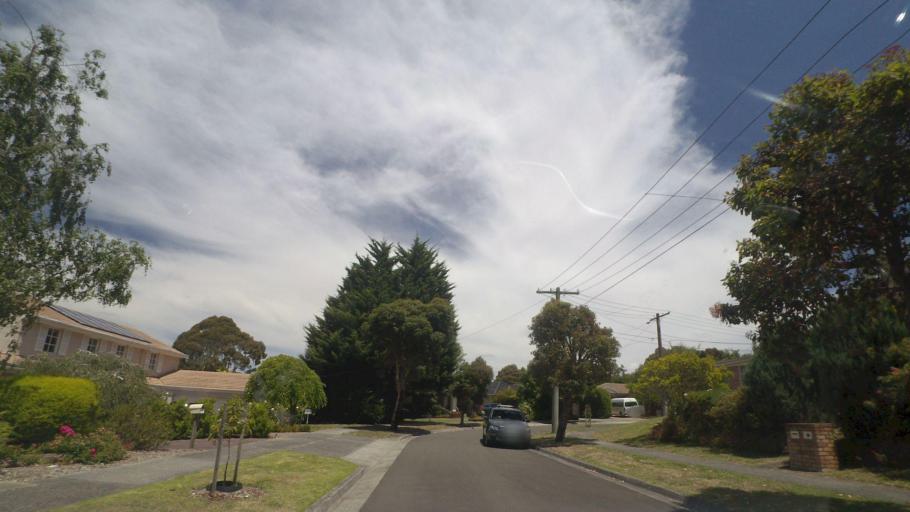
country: AU
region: Victoria
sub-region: Knox
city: Boronia
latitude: -37.8527
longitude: 145.2938
